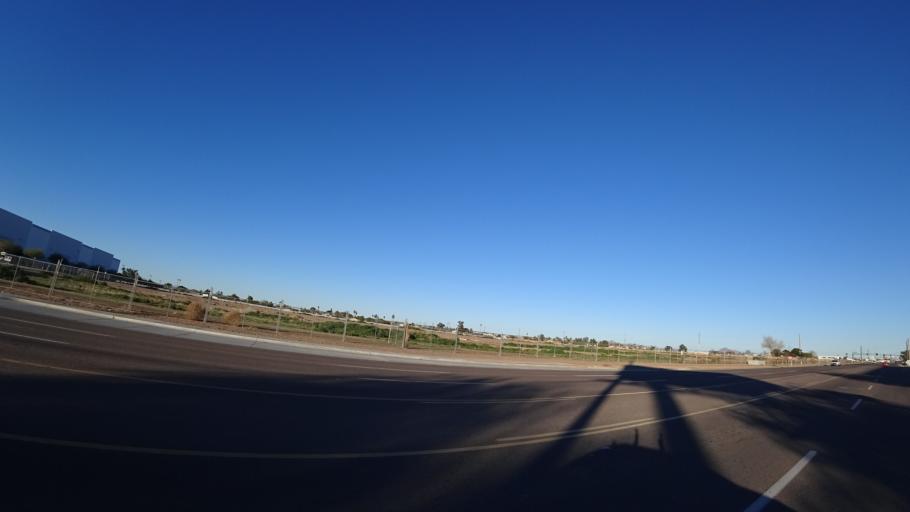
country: US
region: Arizona
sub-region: Maricopa County
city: Tolleson
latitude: 33.4514
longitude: -112.1903
